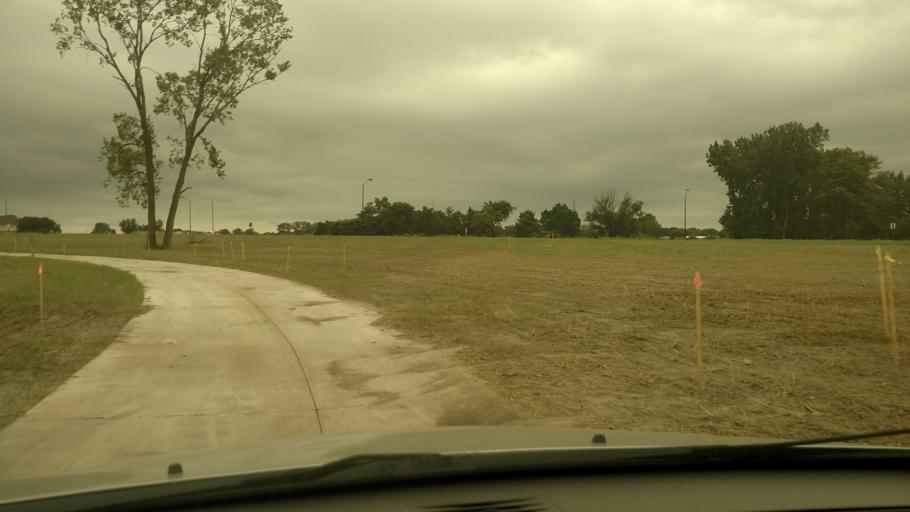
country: US
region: Iowa
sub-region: Polk County
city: Ankeny
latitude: 41.7152
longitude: -93.6139
